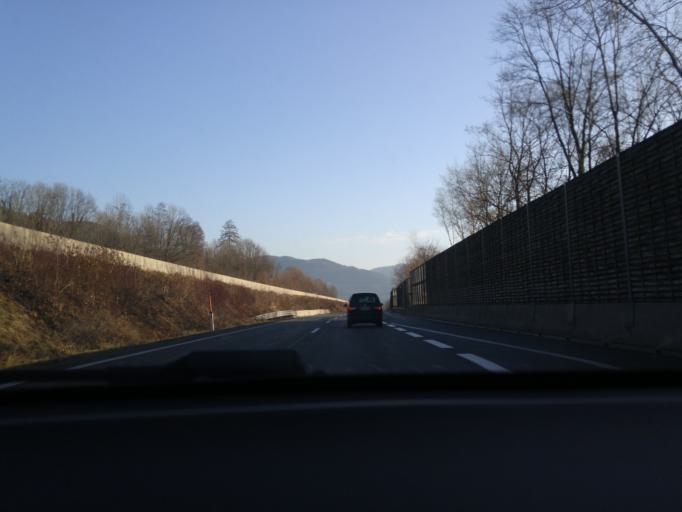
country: AT
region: Upper Austria
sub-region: Politischer Bezirk Vocklabruck
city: Mondsee
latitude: 47.8535
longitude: 13.3603
